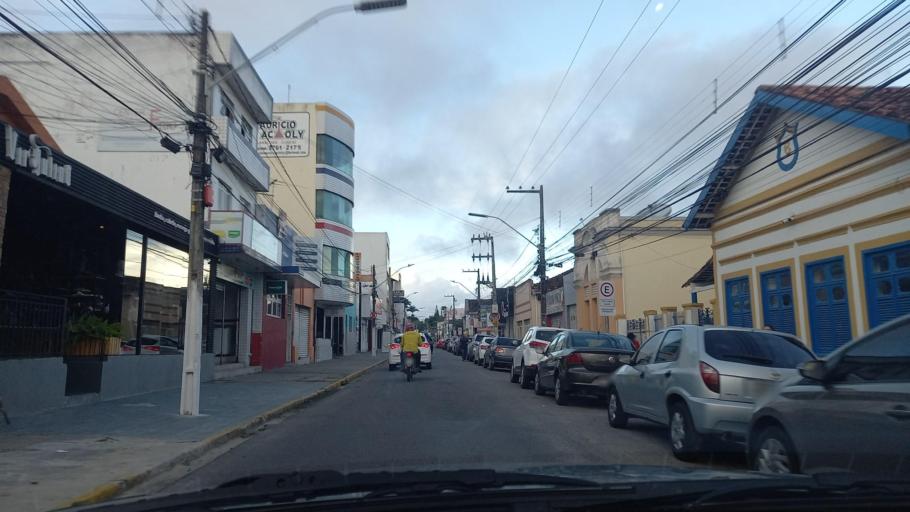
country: BR
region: Pernambuco
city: Garanhuns
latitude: -8.8893
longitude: -36.4919
